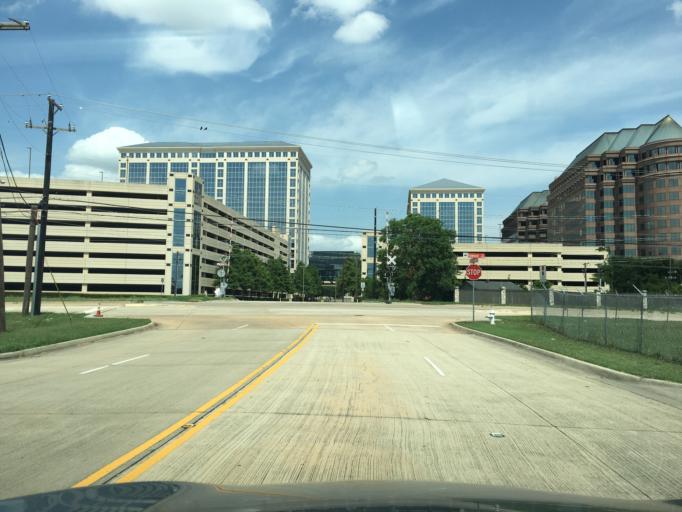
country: US
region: Texas
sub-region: Dallas County
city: Addison
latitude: 32.9407
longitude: -96.8264
